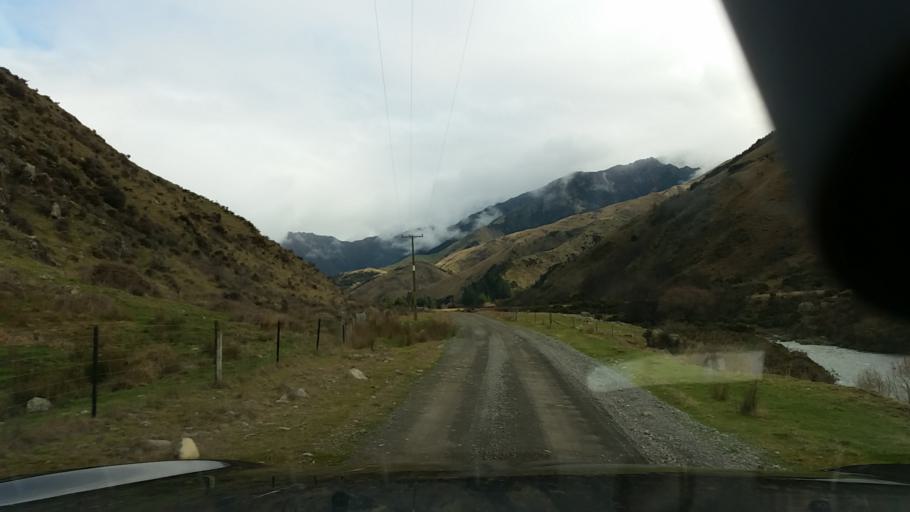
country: NZ
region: Tasman
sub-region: Tasman District
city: Richmond
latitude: -41.7313
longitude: 173.4395
